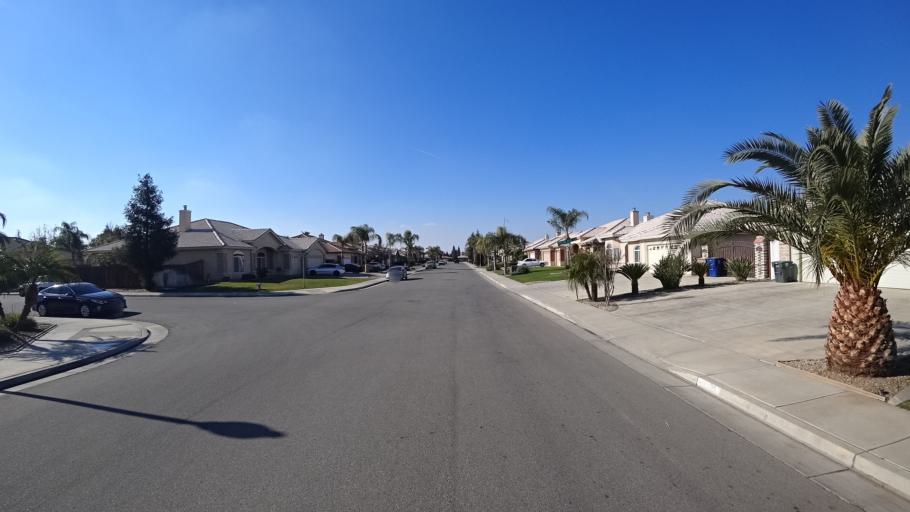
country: US
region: California
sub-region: Kern County
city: Greenfield
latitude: 35.2901
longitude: -119.0395
